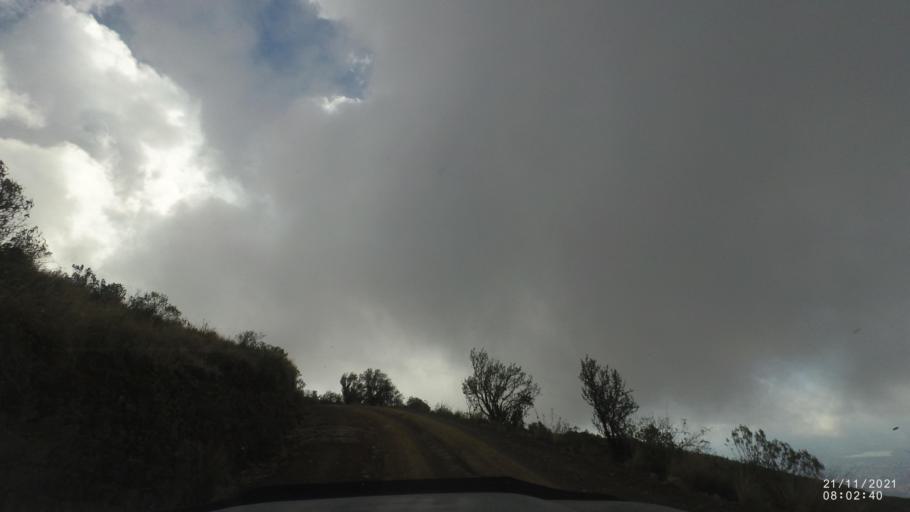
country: BO
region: Cochabamba
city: Cochabamba
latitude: -17.2887
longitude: -66.2145
